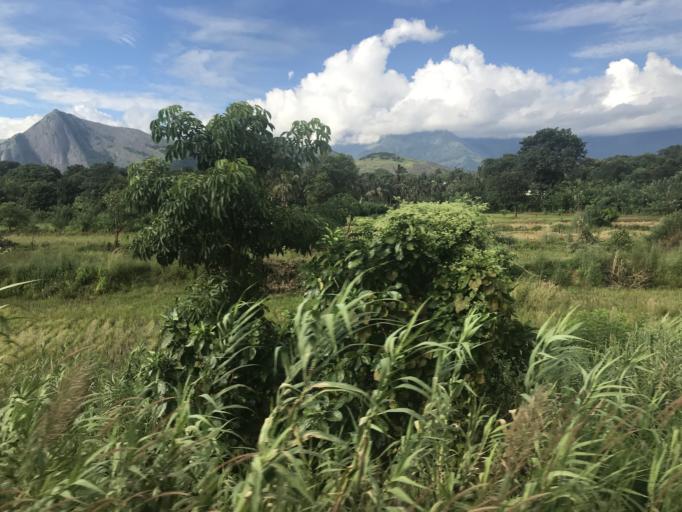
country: IN
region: Kerala
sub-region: Palakkad district
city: Palakkad
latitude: 10.8148
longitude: 76.6713
